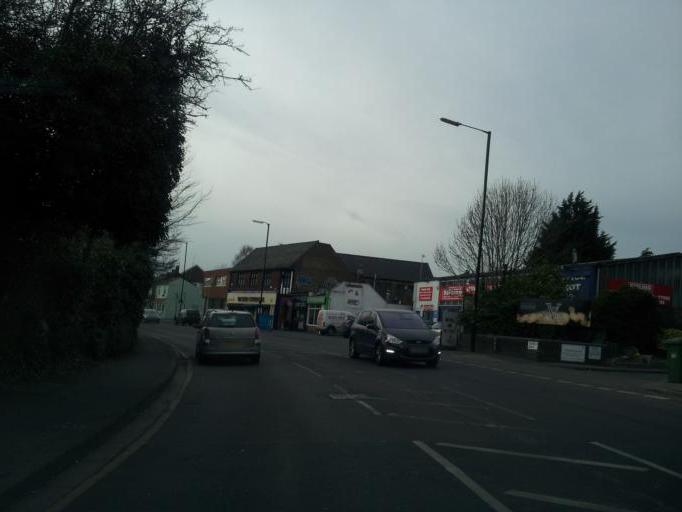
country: GB
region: England
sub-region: Hertfordshire
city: Bushey
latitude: 51.6439
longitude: -0.3613
